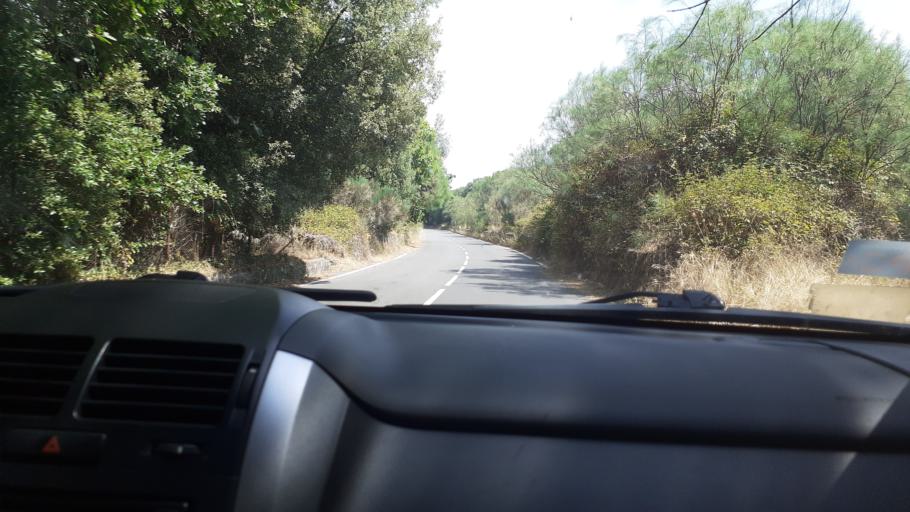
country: IT
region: Sicily
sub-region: Catania
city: Nicolosi
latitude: 37.6450
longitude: 15.0200
